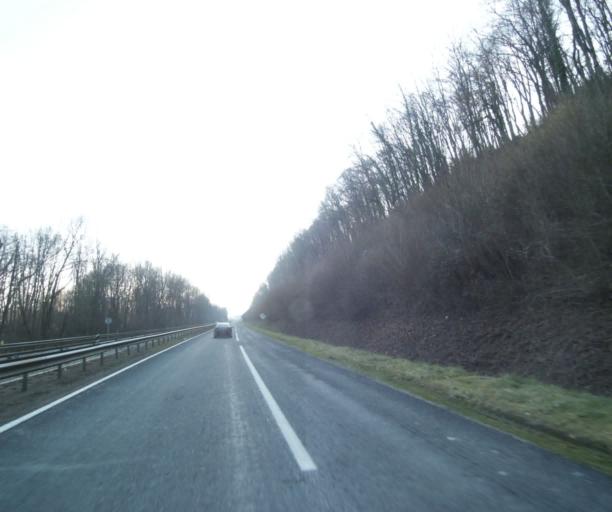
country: FR
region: Champagne-Ardenne
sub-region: Departement de la Haute-Marne
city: Chevillon
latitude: 48.5381
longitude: 5.0984
